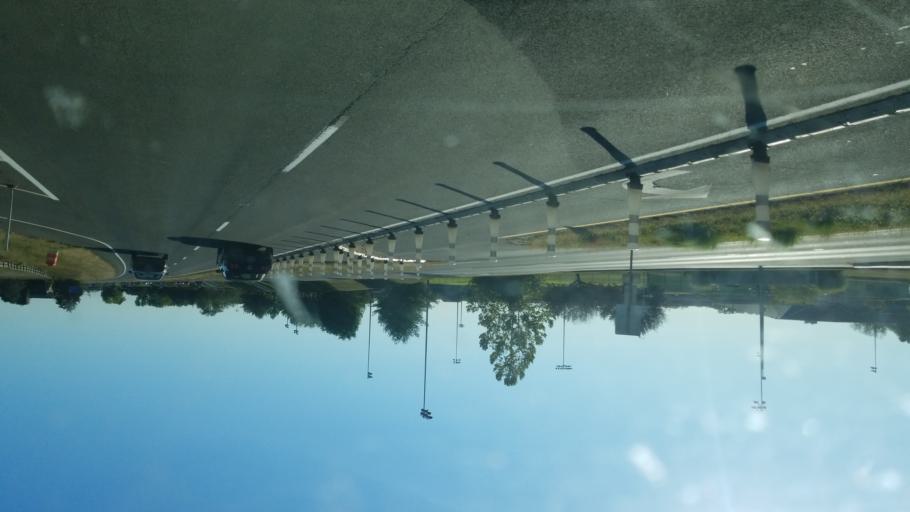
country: US
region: Virginia
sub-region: Fauquier County
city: Bealeton
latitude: 38.5898
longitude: -77.7701
